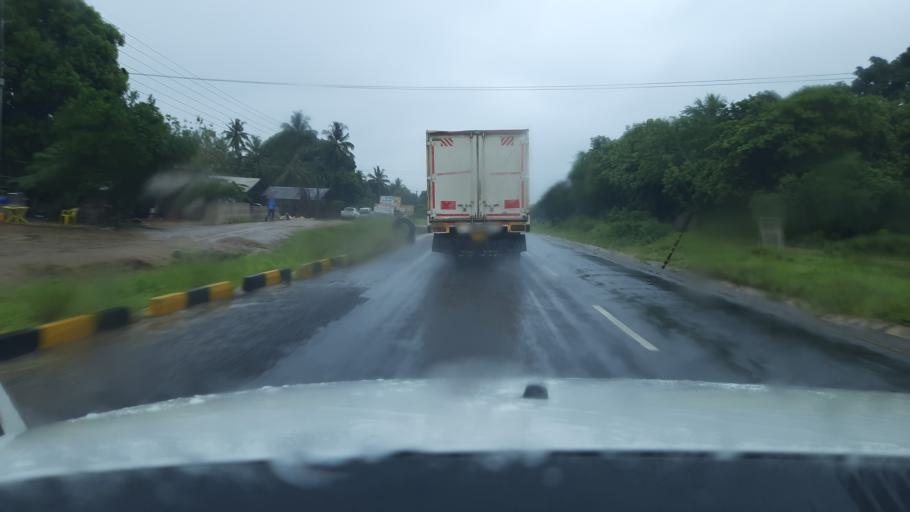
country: TZ
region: Pwani
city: Bagamoyo
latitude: -6.5785
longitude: 39.0292
